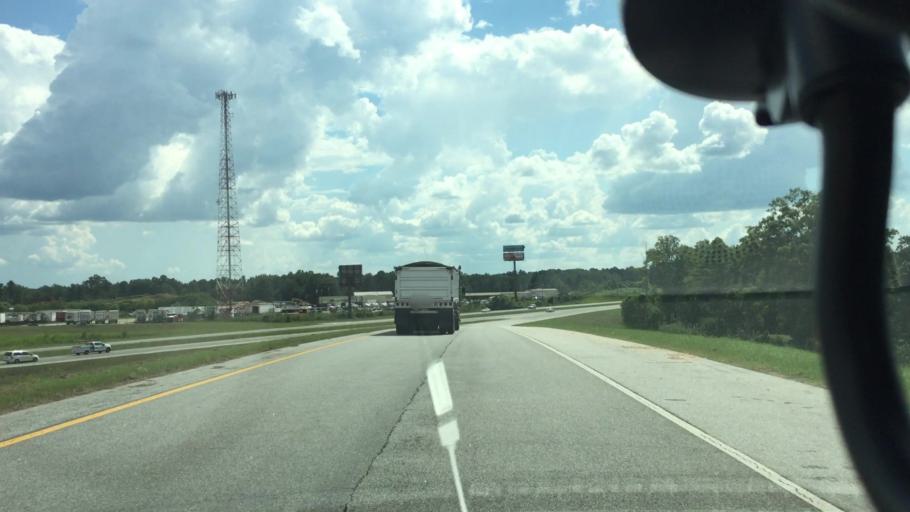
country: US
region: Alabama
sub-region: Lee County
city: Auburn
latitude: 32.5480
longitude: -85.5296
